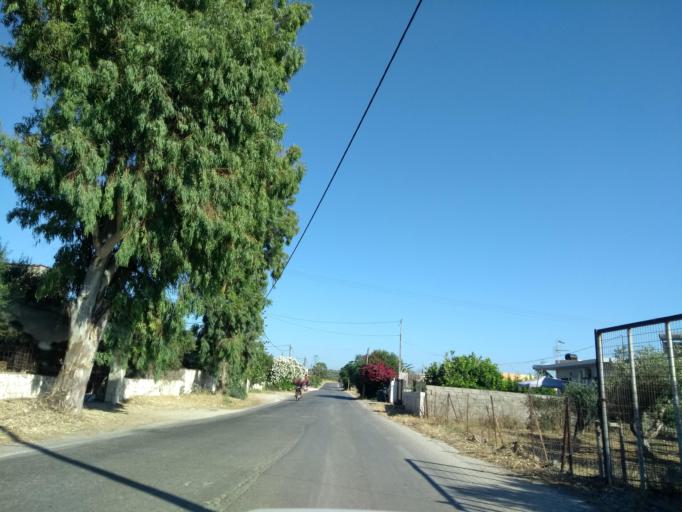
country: GR
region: Crete
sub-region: Nomos Chanias
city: Pithari
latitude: 35.5841
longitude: 24.0899
